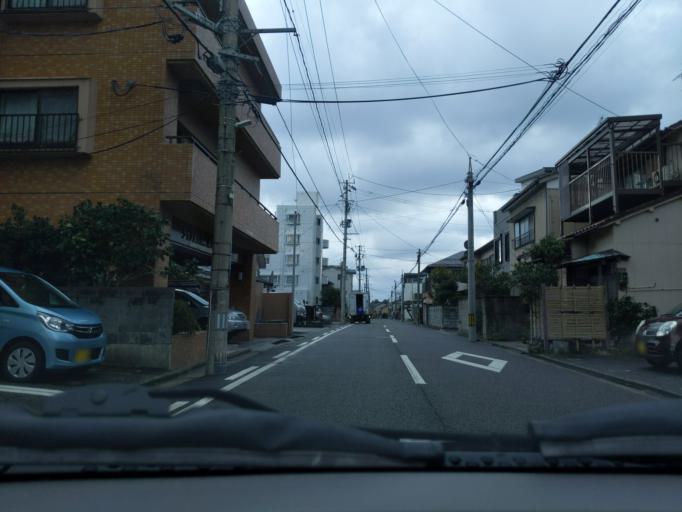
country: JP
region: Niigata
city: Niigata-shi
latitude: 37.9307
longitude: 139.0402
